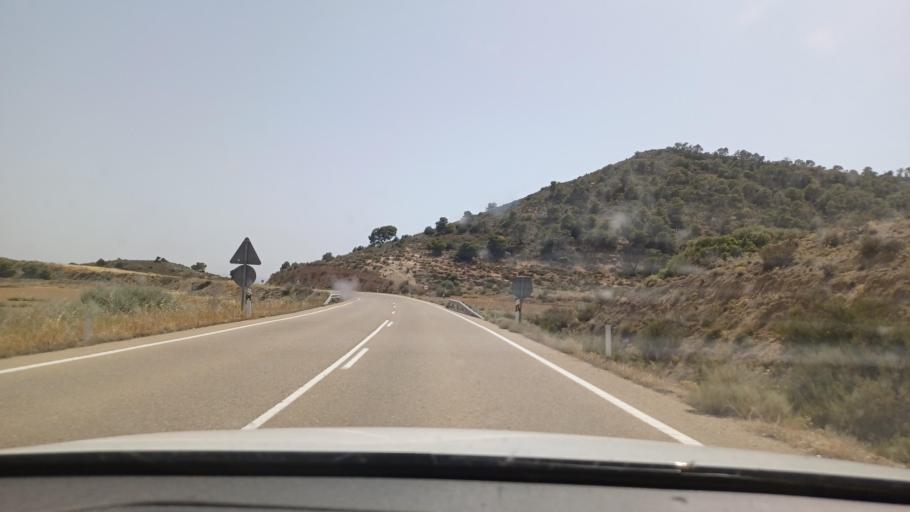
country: ES
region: Aragon
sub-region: Provincia de Zaragoza
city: Chiprana
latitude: 41.3432
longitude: -0.0877
